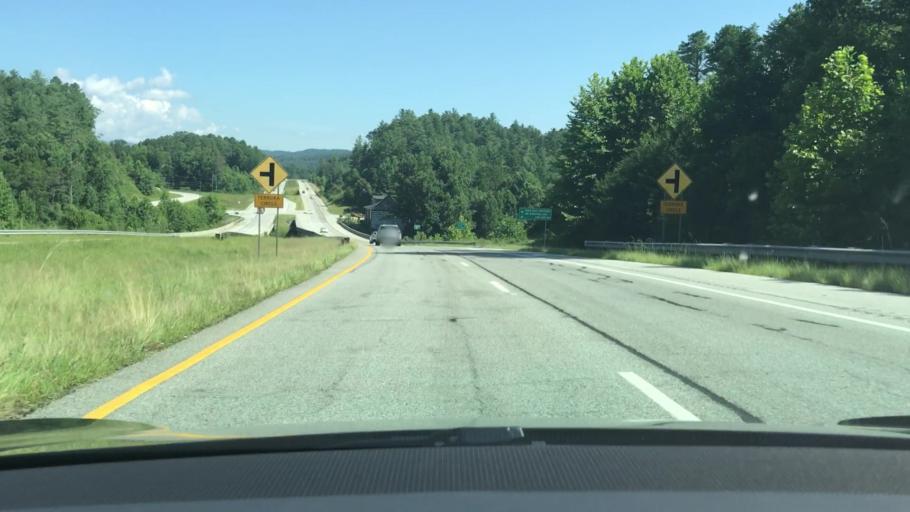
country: US
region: Georgia
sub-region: Rabun County
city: Clayton
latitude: 34.7553
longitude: -83.3963
